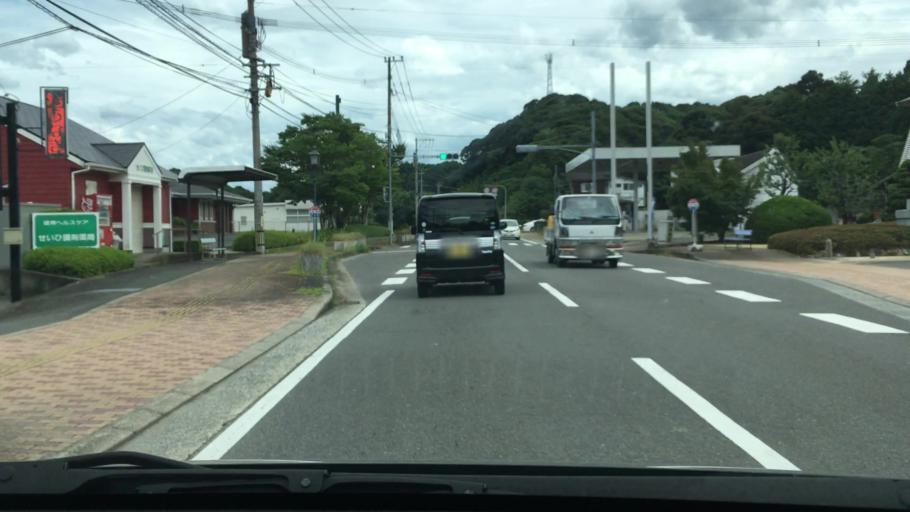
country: JP
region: Nagasaki
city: Sasebo
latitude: 32.9890
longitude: 129.7660
